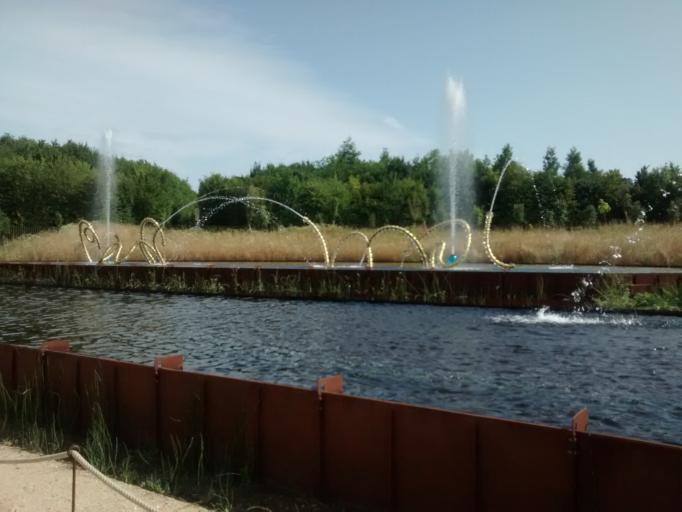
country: FR
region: Ile-de-France
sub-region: Departement des Yvelines
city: Le Chesnay
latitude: 48.8081
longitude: 2.1188
